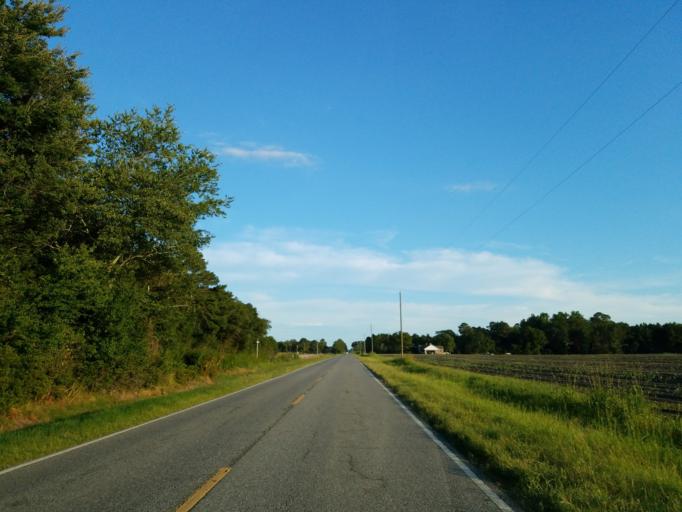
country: US
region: Georgia
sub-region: Tift County
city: Omega
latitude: 31.3200
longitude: -83.4766
